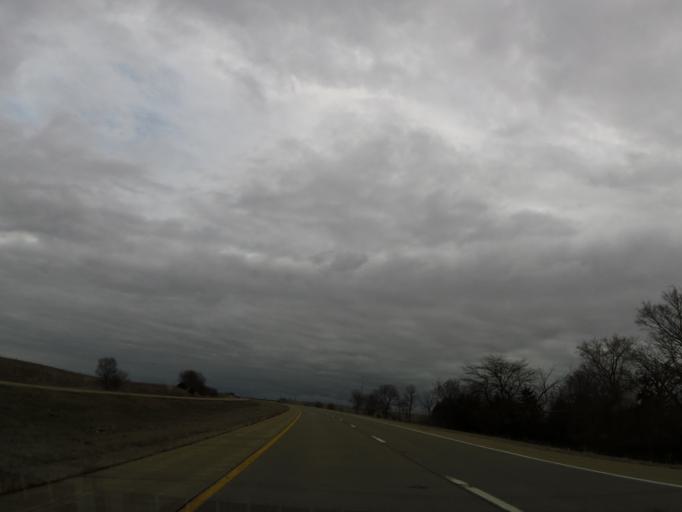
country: US
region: Iowa
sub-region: Buchanan County
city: Jesup
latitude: 42.3593
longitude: -92.0787
